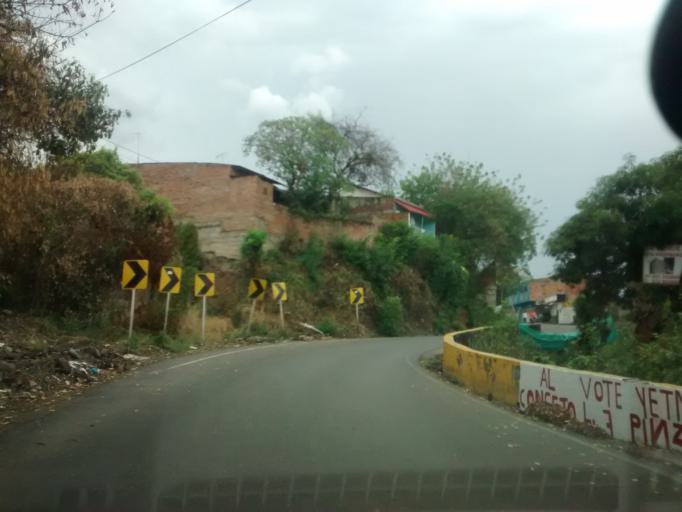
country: CO
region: Cundinamarca
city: Tocaima
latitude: 4.4568
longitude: -74.6372
